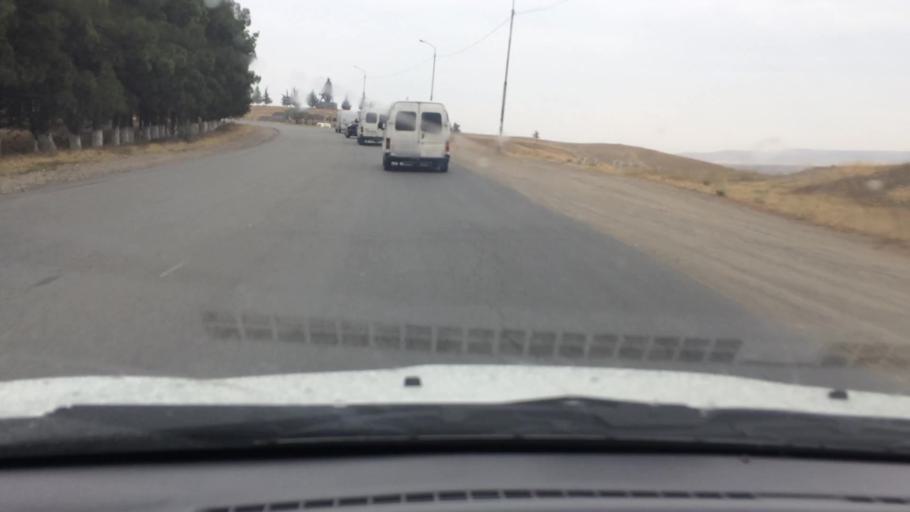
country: GE
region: Kvemo Kartli
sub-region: Marneuli
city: Marneuli
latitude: 41.4991
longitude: 44.8033
